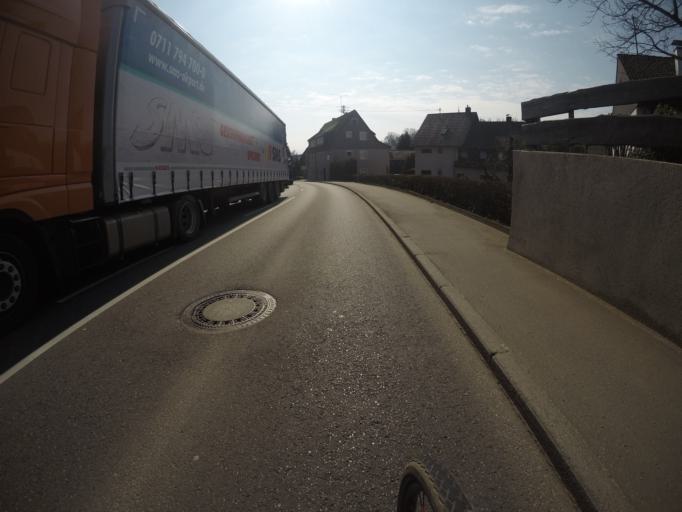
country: DE
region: Baden-Wuerttemberg
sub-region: Regierungsbezirk Stuttgart
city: Nurtingen
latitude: 48.6382
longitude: 9.3195
